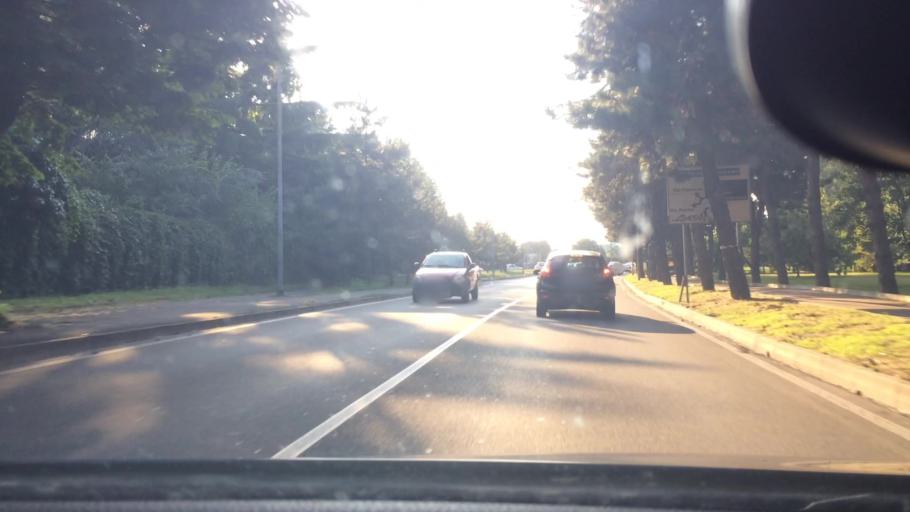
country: IT
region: Lombardy
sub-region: Citta metropolitana di Milano
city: Passirana
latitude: 45.5351
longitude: 9.0251
